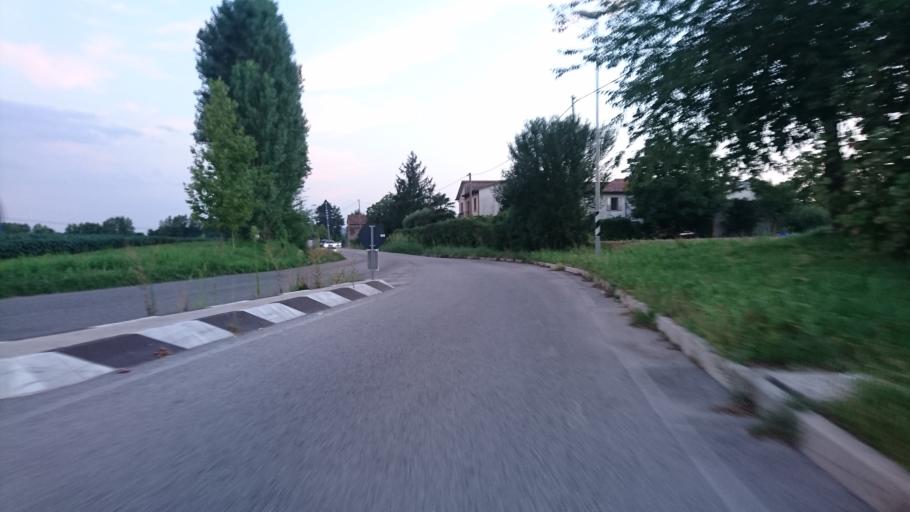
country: IT
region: Veneto
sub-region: Provincia di Padova
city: Selvazzano Dentro
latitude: 45.3774
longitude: 11.8046
